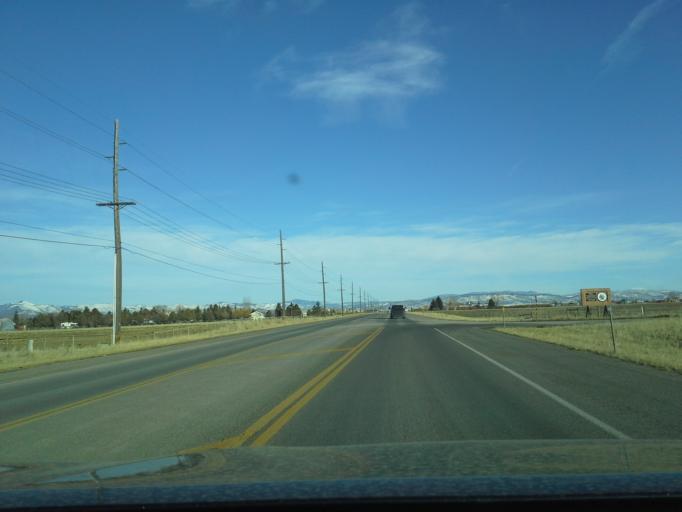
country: US
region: Montana
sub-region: Lewis and Clark County
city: Helena Valley Southeast
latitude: 46.6168
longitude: -111.9541
